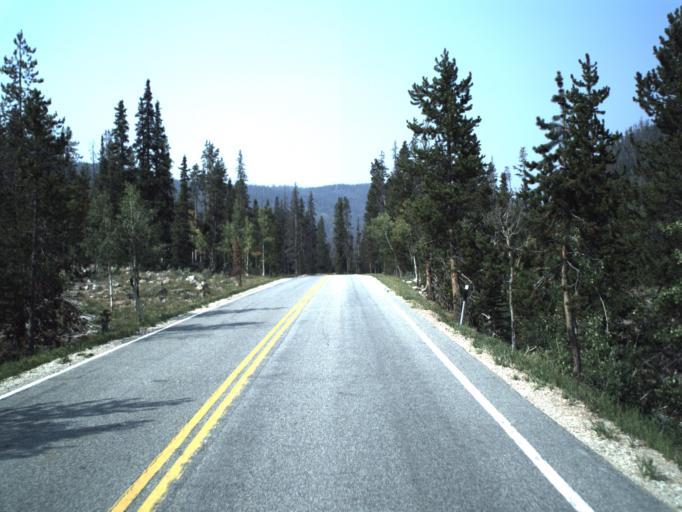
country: US
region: Utah
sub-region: Summit County
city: Francis
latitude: 40.6105
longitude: -110.9618
